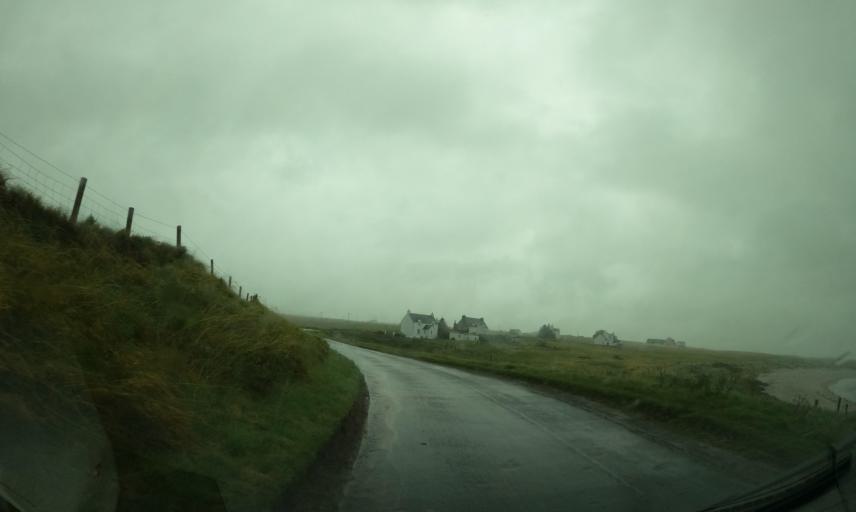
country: GB
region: Scotland
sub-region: Eilean Siar
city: Barra
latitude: 56.4699
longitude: -6.8980
